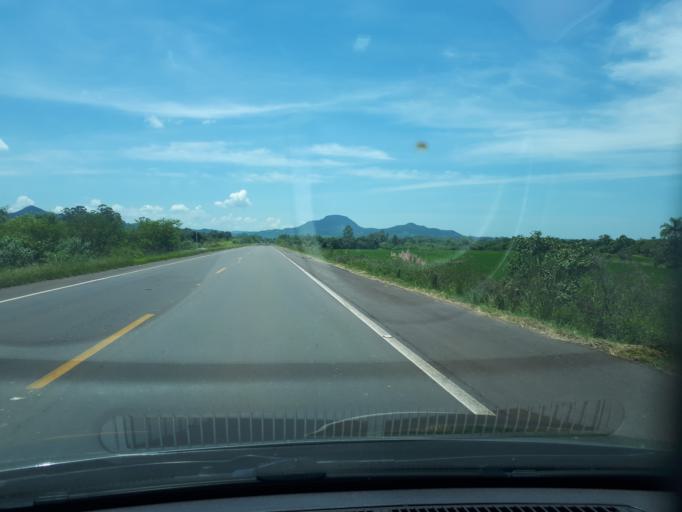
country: BR
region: Rio Grande do Sul
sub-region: Candelaria
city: Candelaria
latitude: -29.7290
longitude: -52.9400
